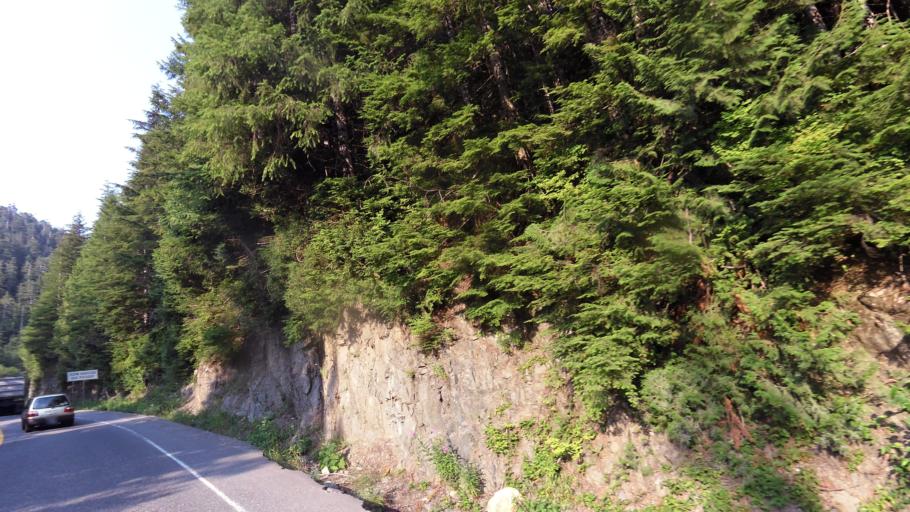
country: CA
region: British Columbia
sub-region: Regional District of Alberni-Clayoquot
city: Ucluelet
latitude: 49.2773
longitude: -125.3588
